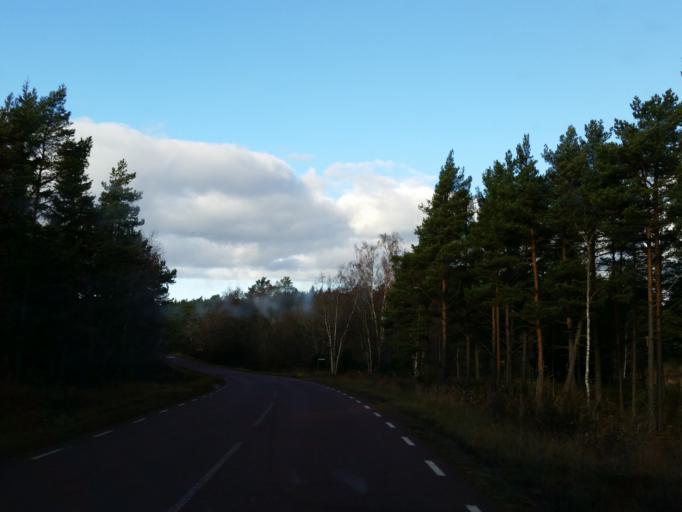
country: AX
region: Alands skaergard
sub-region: Foegloe
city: Foegloe
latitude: 60.0459
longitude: 20.5326
